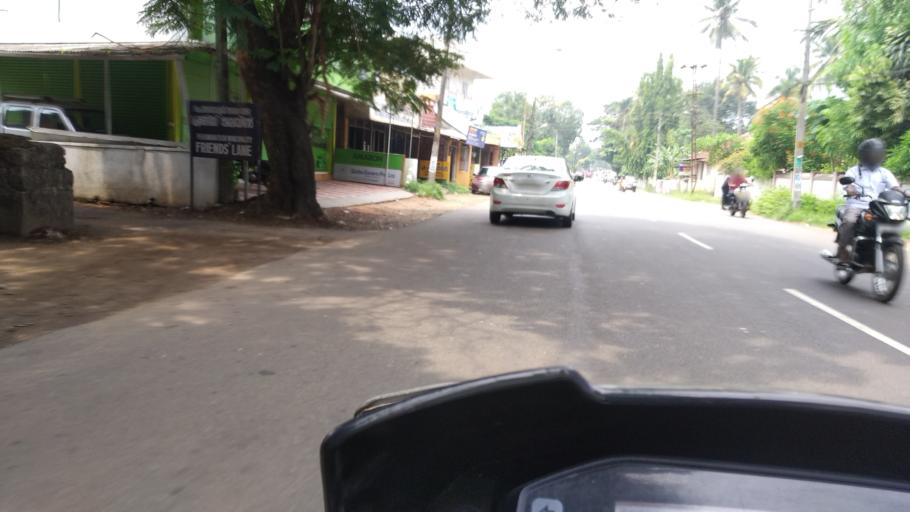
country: IN
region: Kerala
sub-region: Ernakulam
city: Perumpavur
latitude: 10.1160
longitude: 76.4837
